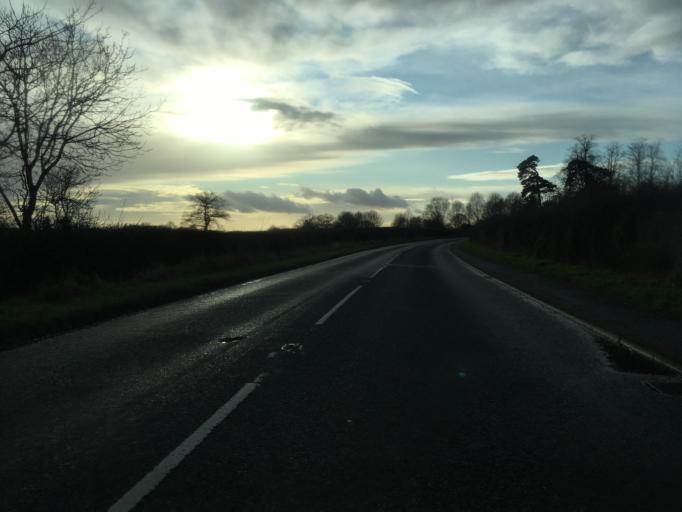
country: GB
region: England
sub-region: Warwickshire
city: Alcester
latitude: 52.2230
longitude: -1.8524
